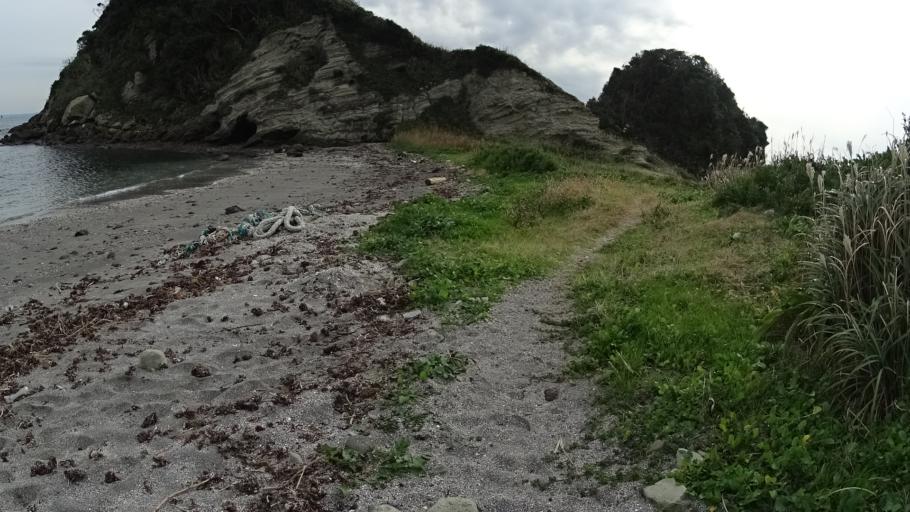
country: JP
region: Kanagawa
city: Miura
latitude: 35.1388
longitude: 139.6567
